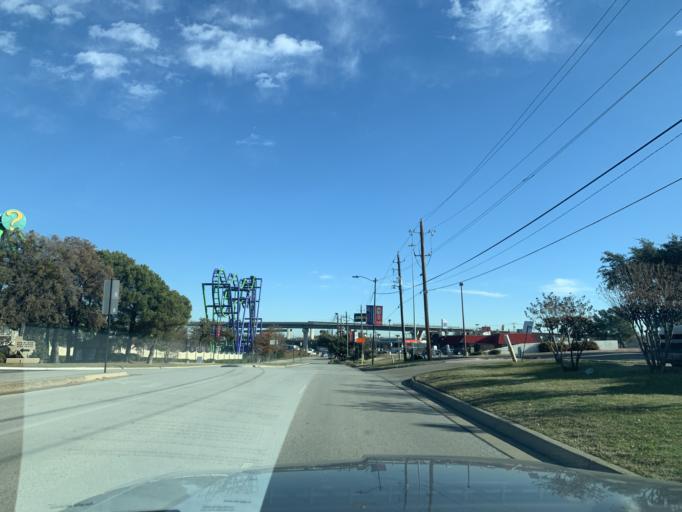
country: US
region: Texas
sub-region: Tarrant County
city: Arlington
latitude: 32.7558
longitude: -97.0666
